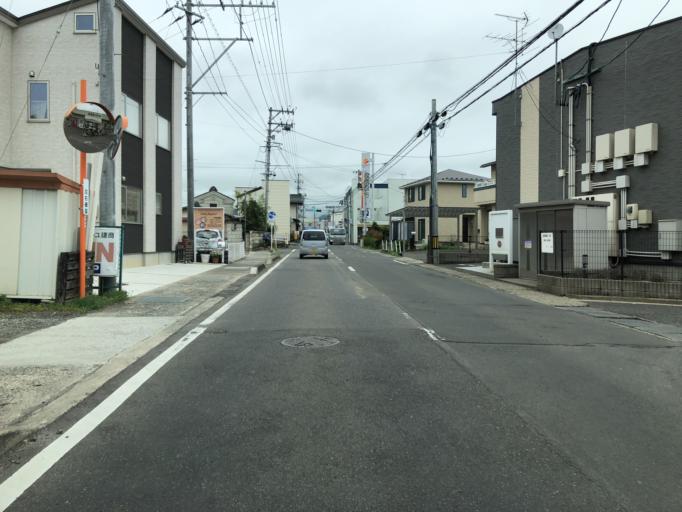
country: JP
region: Fukushima
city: Fukushima-shi
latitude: 37.7691
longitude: 140.4290
